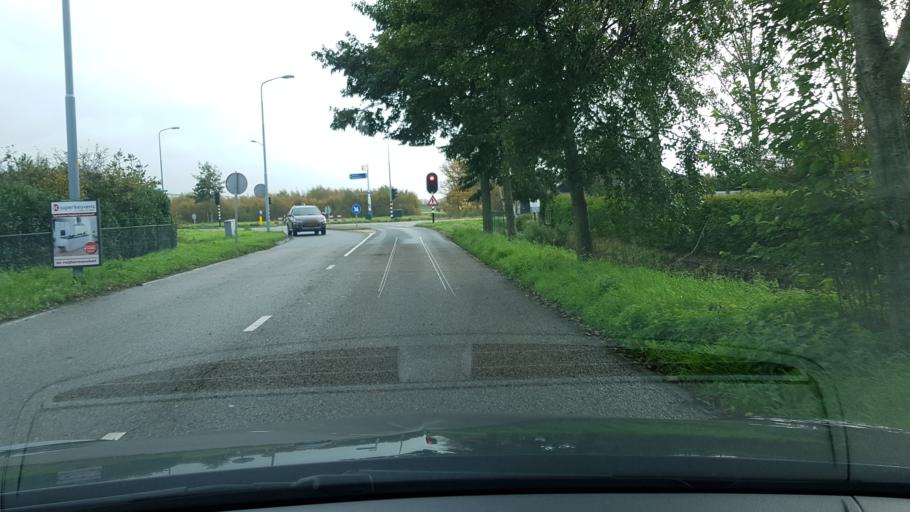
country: NL
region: North Holland
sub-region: Gemeente Heemstede
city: Heemstede
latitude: 52.3274
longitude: 4.6432
